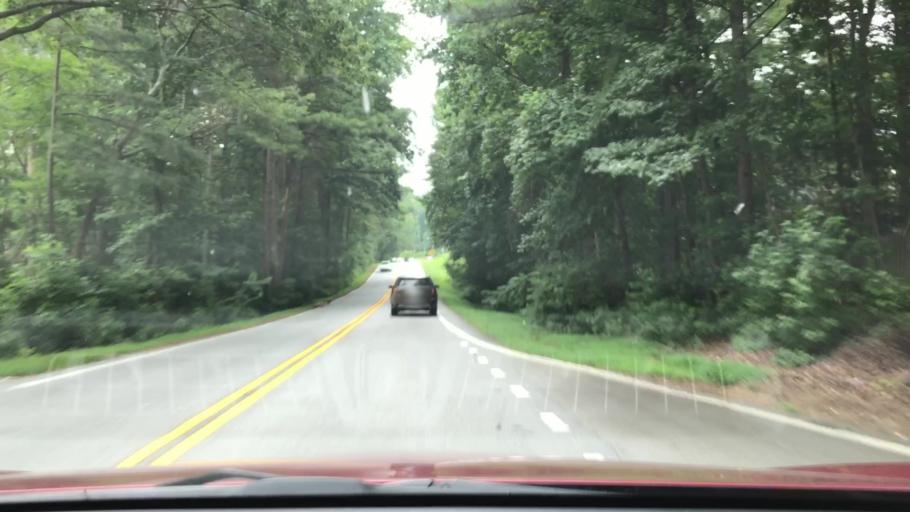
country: US
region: Georgia
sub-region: Gwinnett County
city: Suwanee
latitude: 34.0009
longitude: -84.0565
